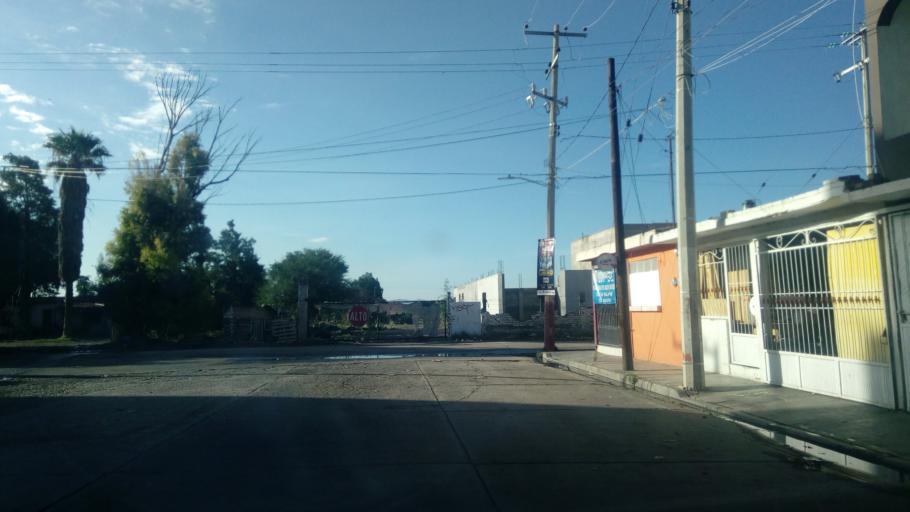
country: MX
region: Durango
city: Victoria de Durango
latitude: 24.0514
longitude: -104.6064
